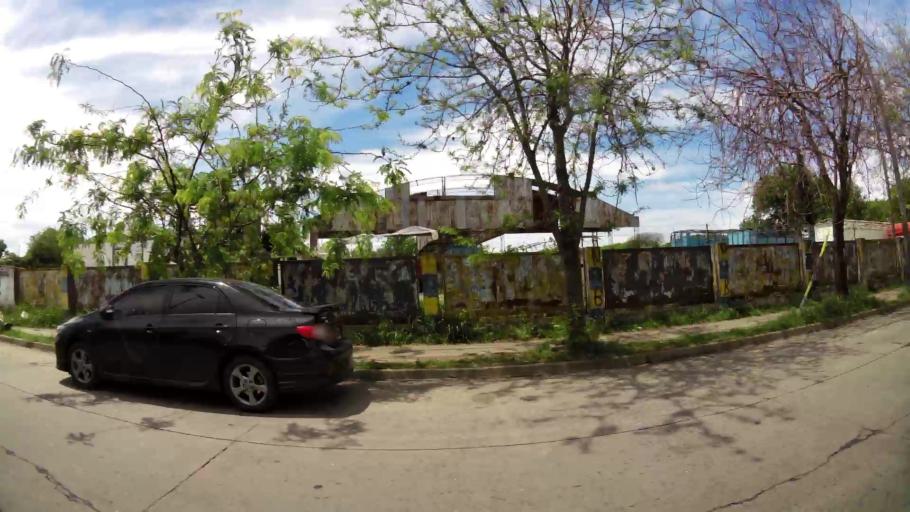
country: AR
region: Santa Fe
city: Gobernador Galvez
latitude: -32.9891
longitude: -60.6284
